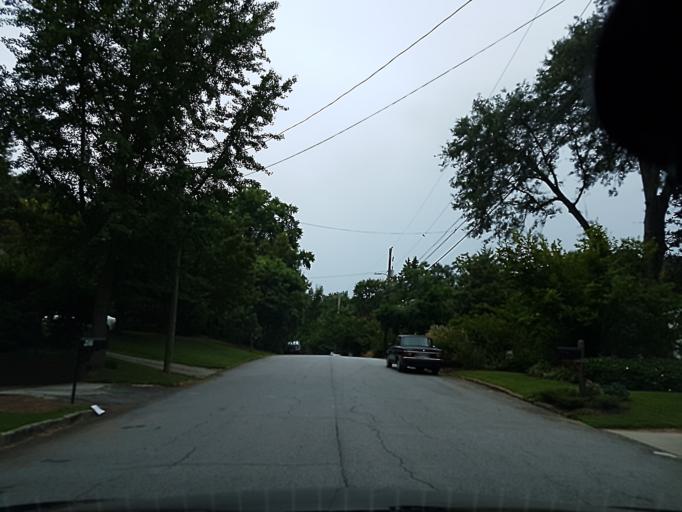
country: US
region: Georgia
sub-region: DeKalb County
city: North Decatur
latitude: 33.7889
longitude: -84.2951
